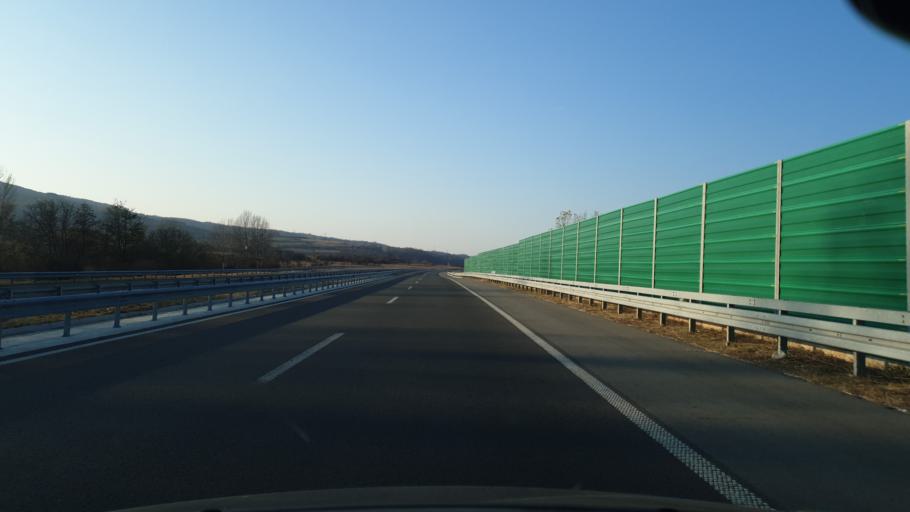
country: RS
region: Central Serbia
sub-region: Pirotski Okrug
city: Dimitrovgrad
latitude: 43.0358
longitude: 22.7174
